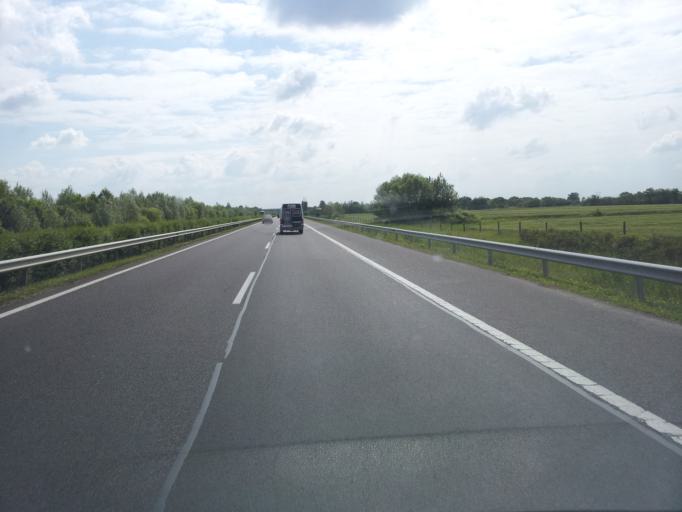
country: HU
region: Borsod-Abauj-Zemplen
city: Hejobaba
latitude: 47.8745
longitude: 20.9379
